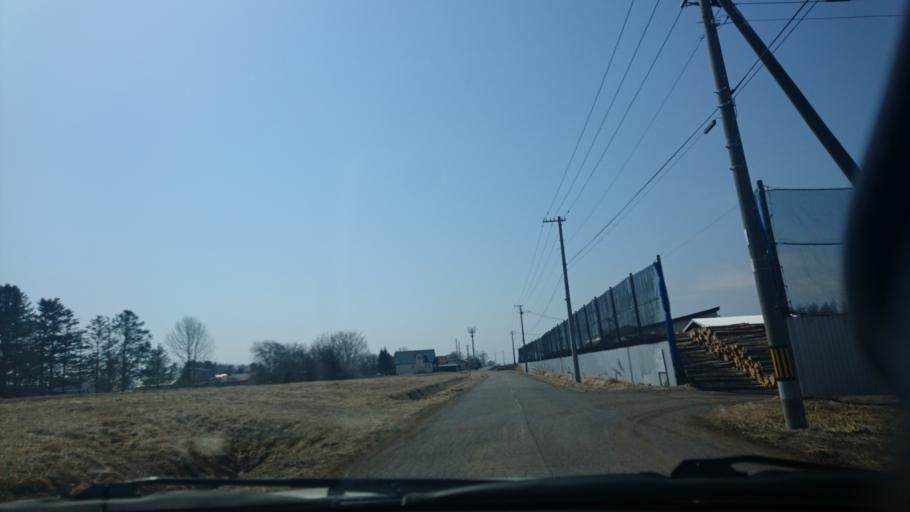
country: JP
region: Hokkaido
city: Otofuke
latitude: 43.0963
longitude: 143.2259
